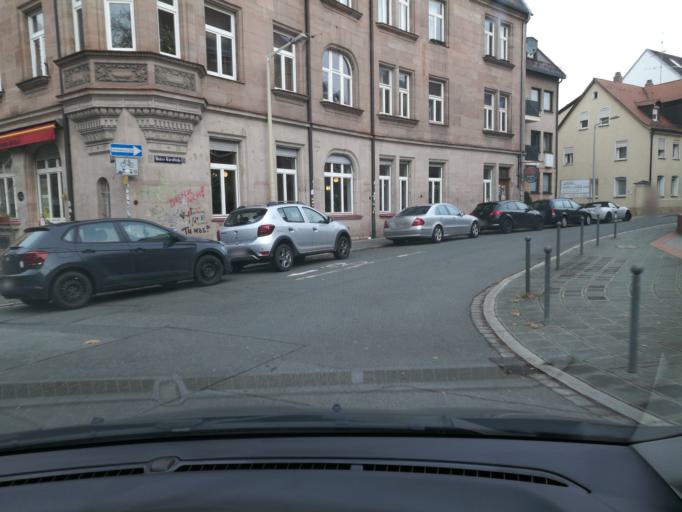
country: DE
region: Bavaria
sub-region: Regierungsbezirk Mittelfranken
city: Nuernberg
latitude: 49.4522
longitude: 11.0645
